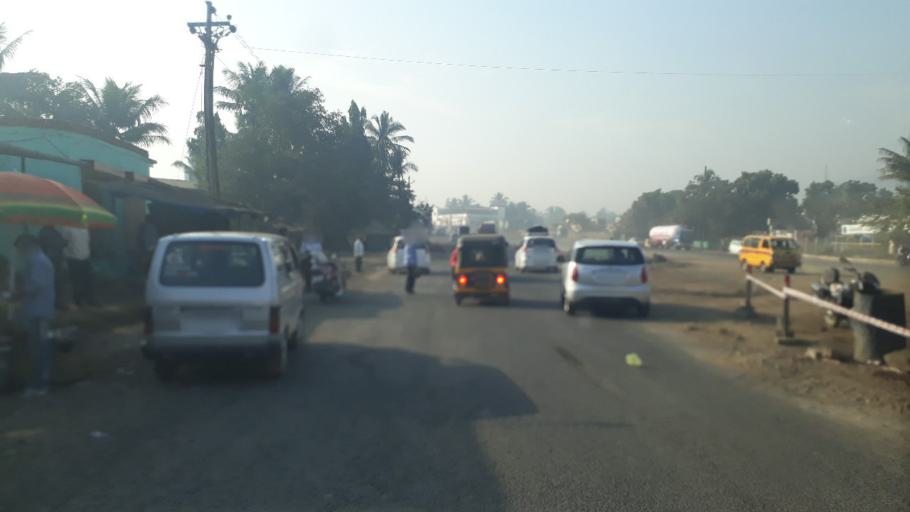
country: IN
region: Maharashtra
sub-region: Raigarh
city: Kalundri
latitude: 18.9594
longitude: 73.1312
